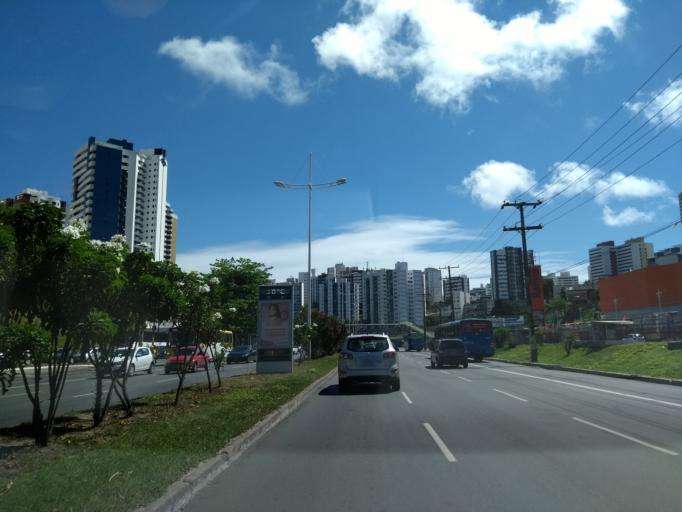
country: BR
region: Bahia
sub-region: Salvador
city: Salvador
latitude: -12.9904
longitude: -38.4736
